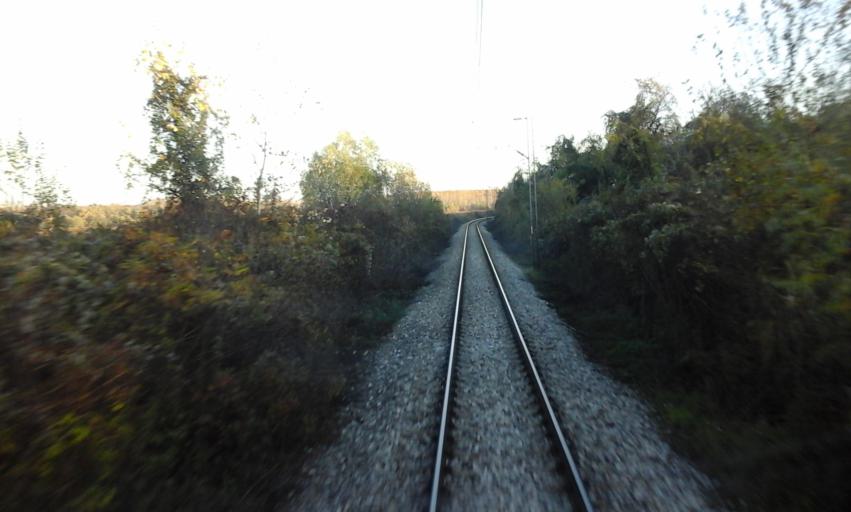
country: RS
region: Autonomna Pokrajina Vojvodina
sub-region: Juznobacki Okrug
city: Petrovaradin
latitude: 45.2222
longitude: 19.9042
